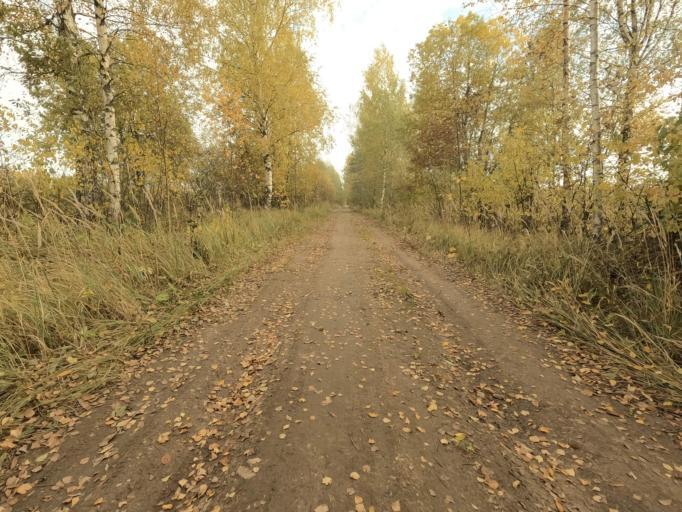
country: RU
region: Novgorod
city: Pankovka
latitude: 58.8798
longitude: 30.8094
